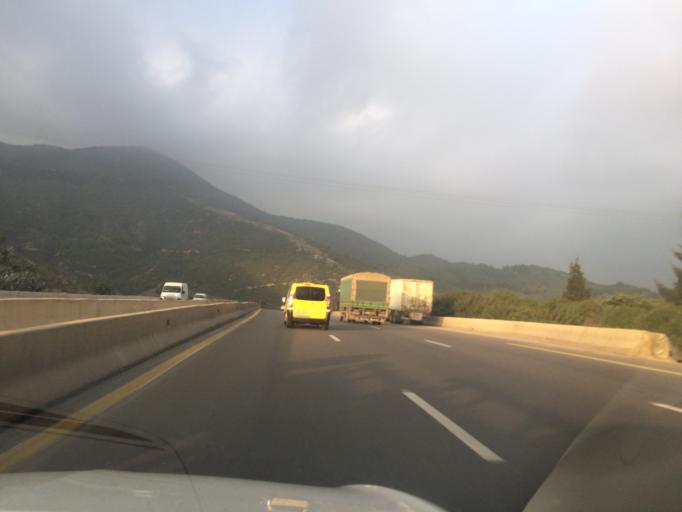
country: DZ
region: Tipaza
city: El Affroun
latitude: 36.3983
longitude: 2.5379
